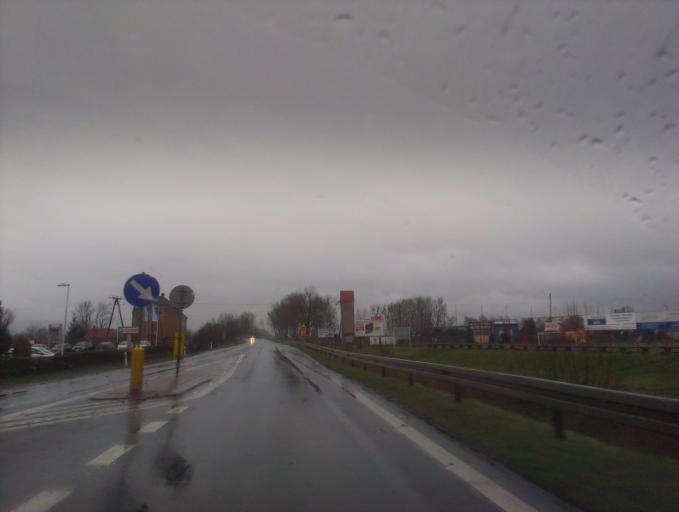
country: PL
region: Greater Poland Voivodeship
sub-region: Powiat pilski
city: Ujscie
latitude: 53.0617
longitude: 16.7287
